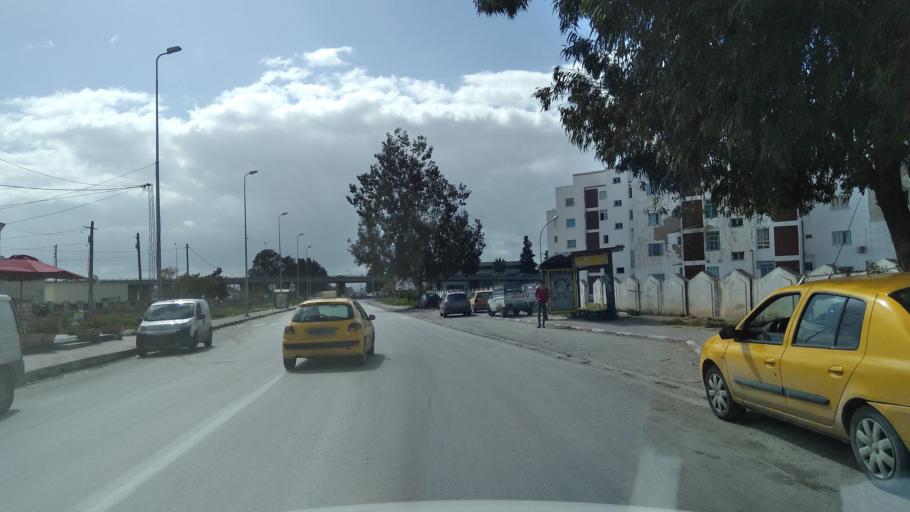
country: TN
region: Bin 'Arus
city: Ben Arous
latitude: 36.7432
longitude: 10.2262
